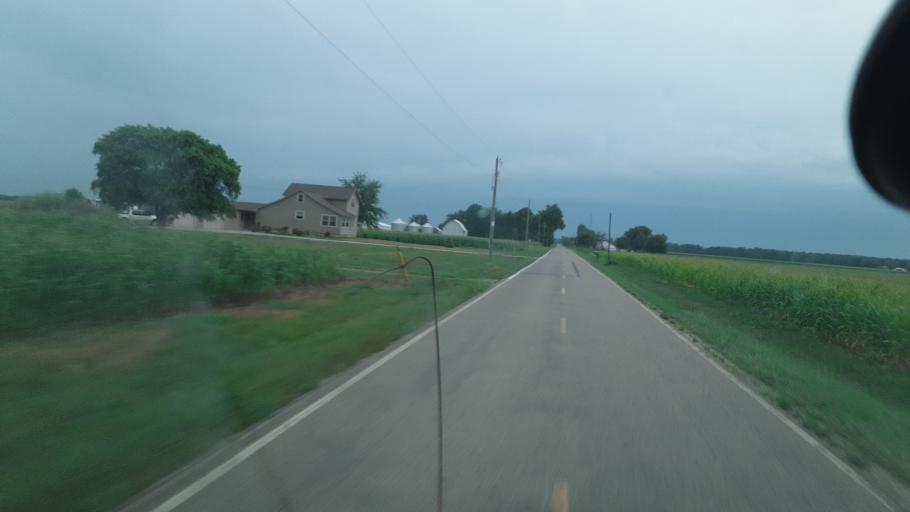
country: US
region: Ohio
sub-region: Defiance County
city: Hicksville
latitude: 41.2670
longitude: -84.7403
